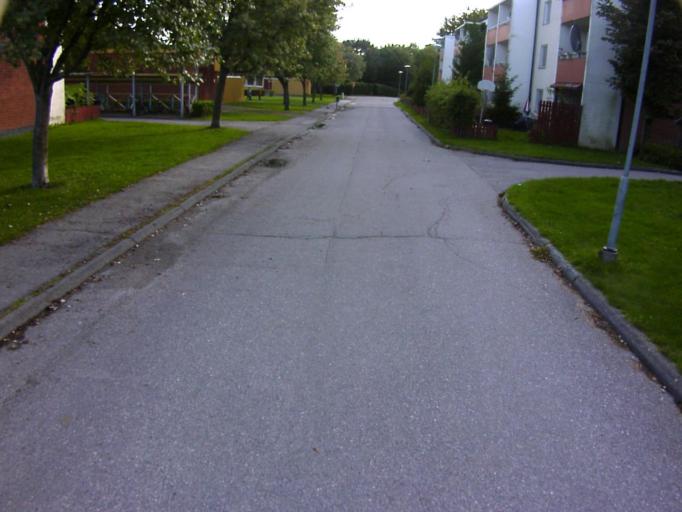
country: SE
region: Soedermanland
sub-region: Eskilstuna Kommun
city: Eskilstuna
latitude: 59.3914
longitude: 16.5391
